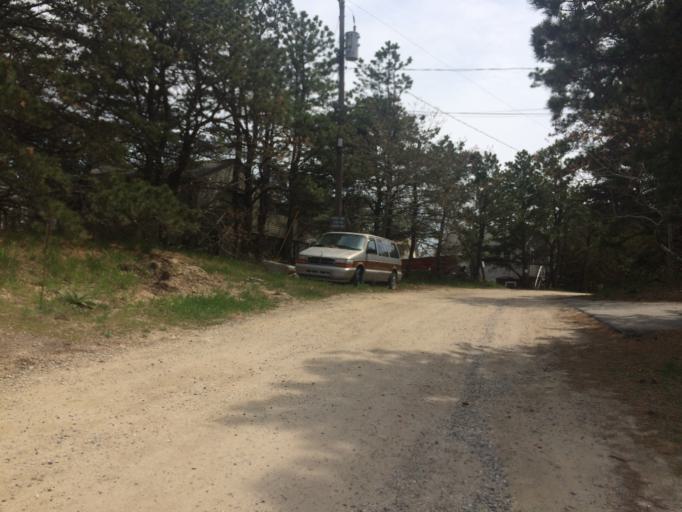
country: US
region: Massachusetts
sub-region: Barnstable County
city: Provincetown
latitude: 42.0520
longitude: -70.1970
